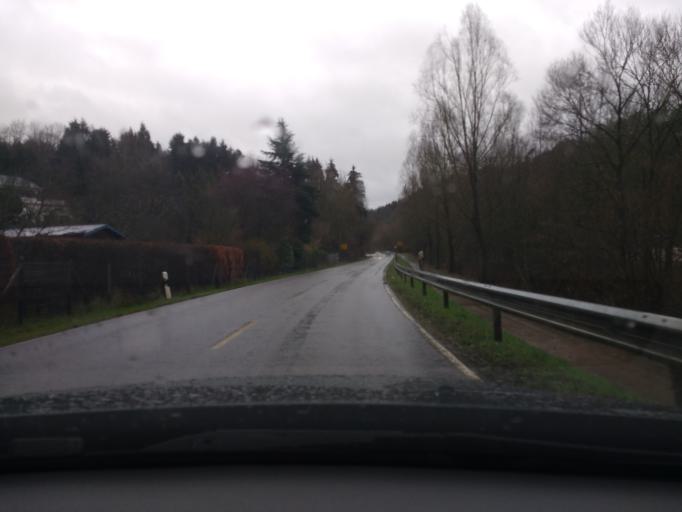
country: DE
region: Rheinland-Pfalz
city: Irsch
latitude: 49.7386
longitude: 6.6750
